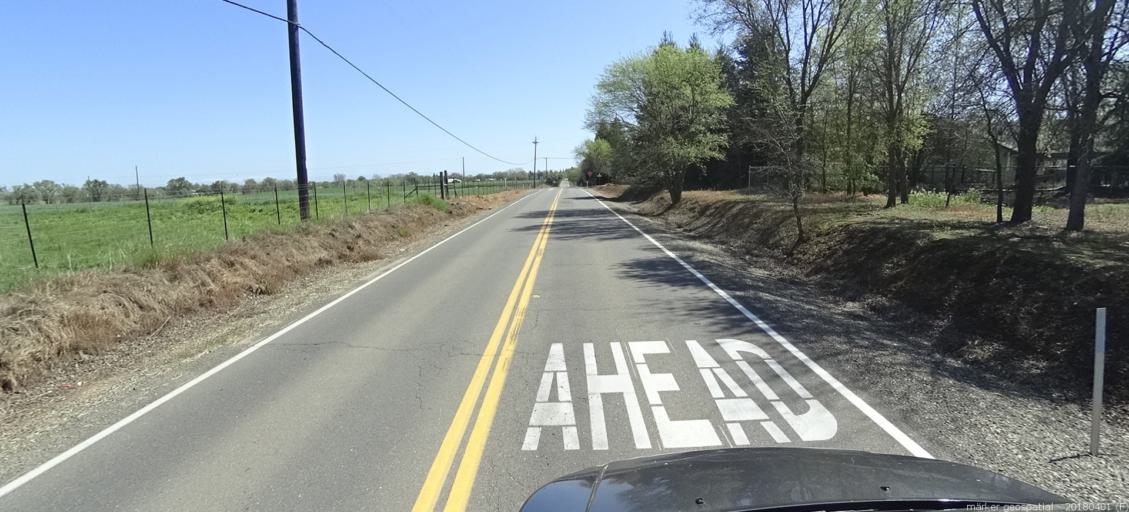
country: US
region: California
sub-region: Sacramento County
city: Wilton
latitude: 38.4186
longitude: -121.2465
